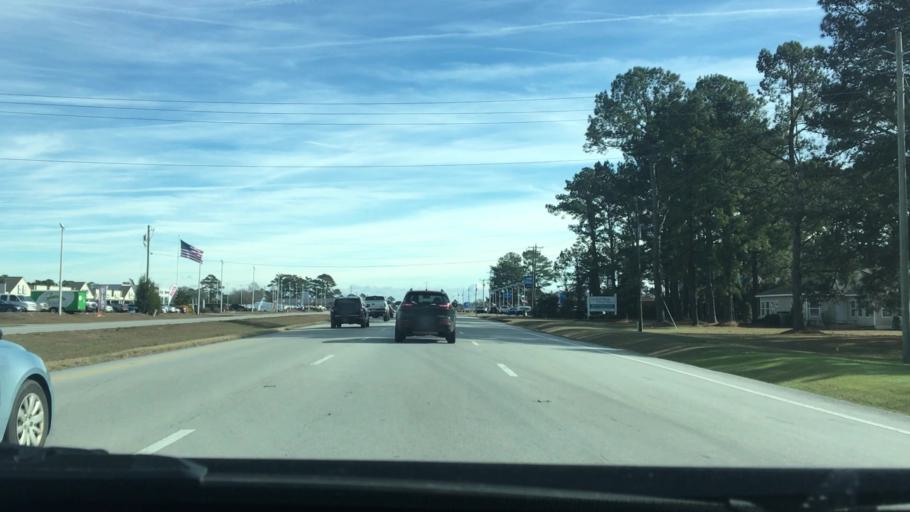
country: US
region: North Carolina
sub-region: Carteret County
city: Pine Knoll Shores
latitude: 34.7433
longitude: -76.8245
